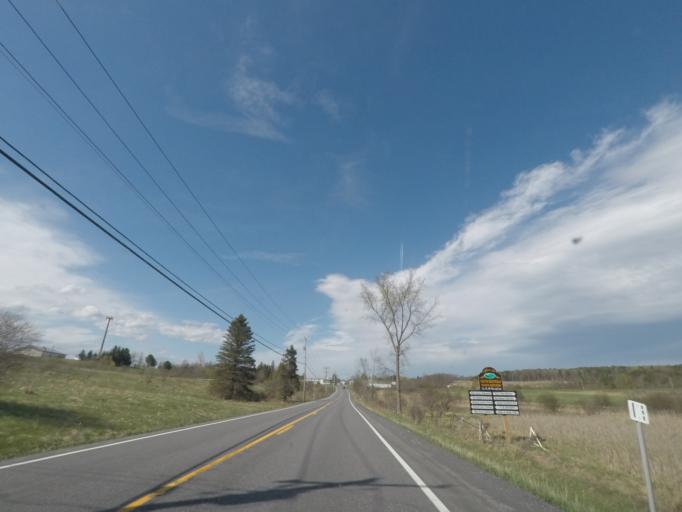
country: US
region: New York
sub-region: Greene County
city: Cairo
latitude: 42.4395
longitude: -74.0170
